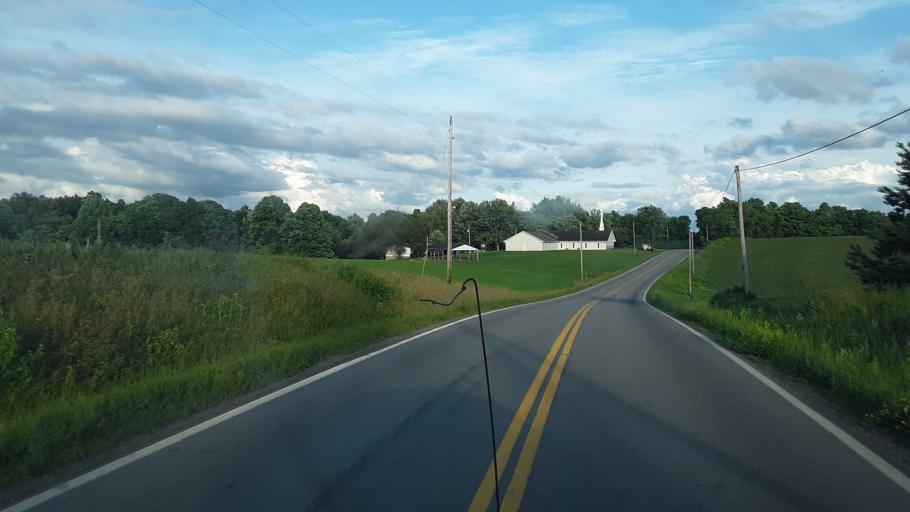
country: US
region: Ohio
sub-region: Carroll County
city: Carrollton
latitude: 40.4525
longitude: -80.9879
